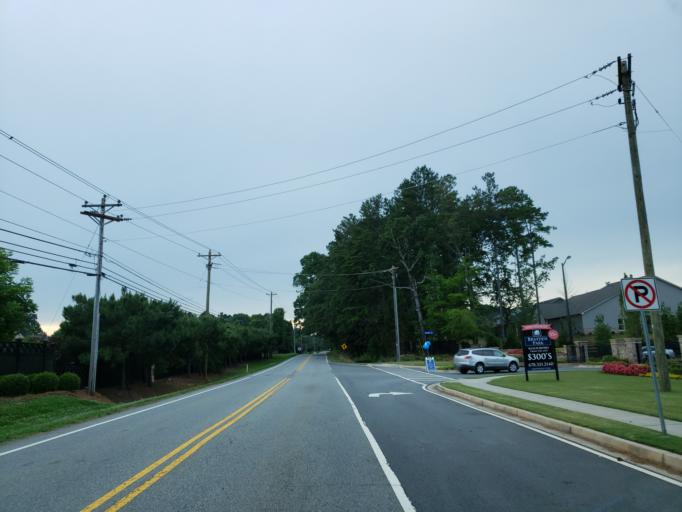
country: US
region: Georgia
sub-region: Cherokee County
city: Ball Ground
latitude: 34.2437
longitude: -84.3541
